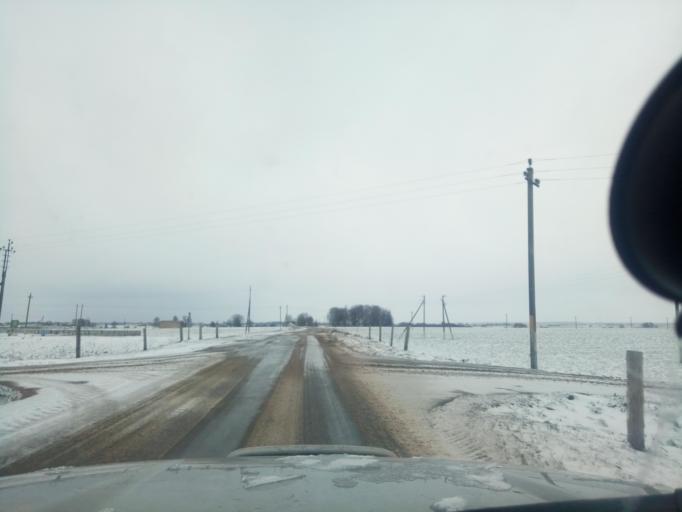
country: BY
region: Minsk
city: Klyetsk
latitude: 53.0384
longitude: 26.7424
